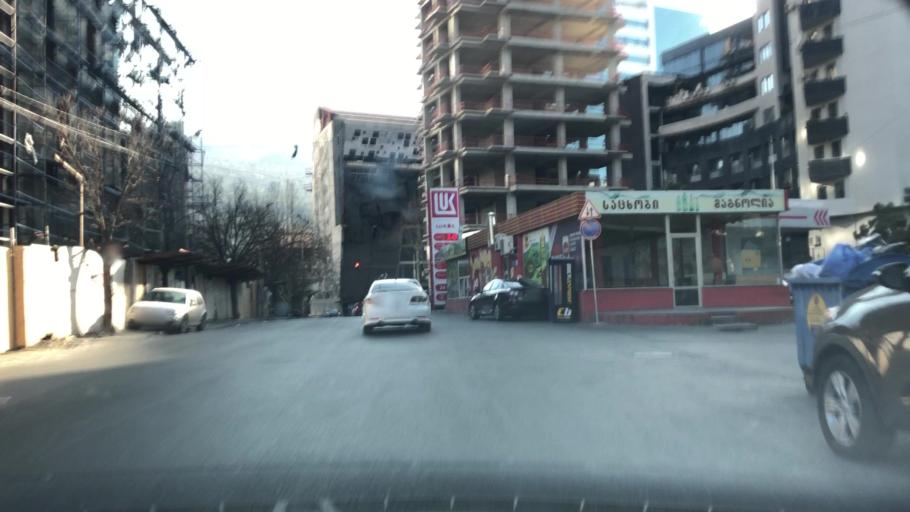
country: GE
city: Tsqnet'i
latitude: 41.7125
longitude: 44.7563
